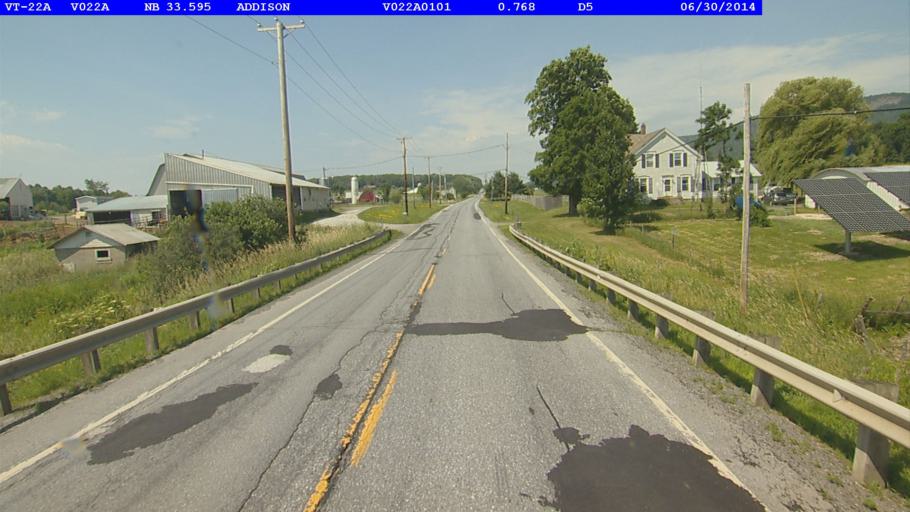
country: US
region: Vermont
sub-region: Addison County
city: Vergennes
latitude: 44.0409
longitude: -73.3054
